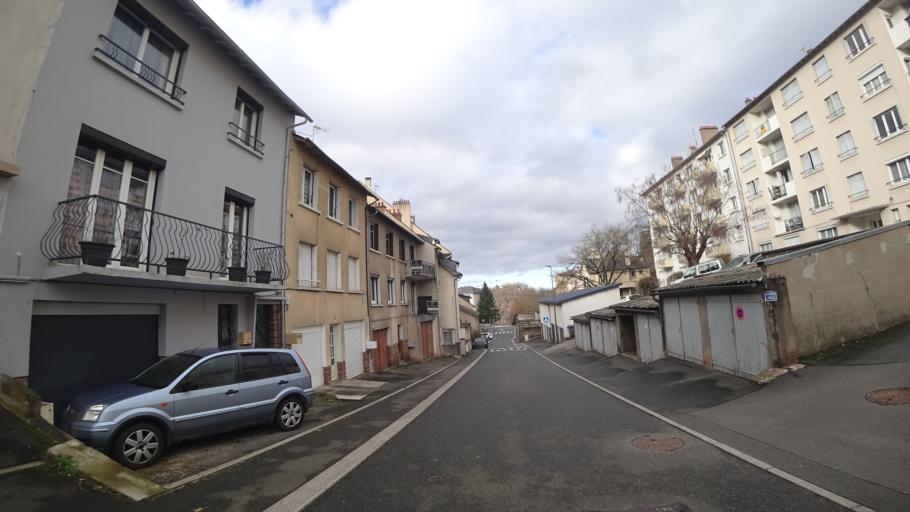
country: FR
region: Midi-Pyrenees
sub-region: Departement de l'Aveyron
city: Rodez
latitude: 44.3560
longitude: 2.5700
